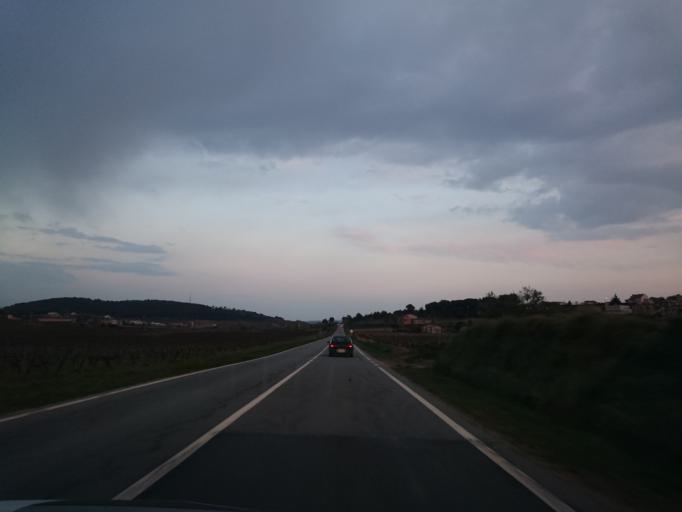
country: ES
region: Catalonia
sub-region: Provincia de Barcelona
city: Vilobi del Penedes
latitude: 41.3682
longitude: 1.6535
